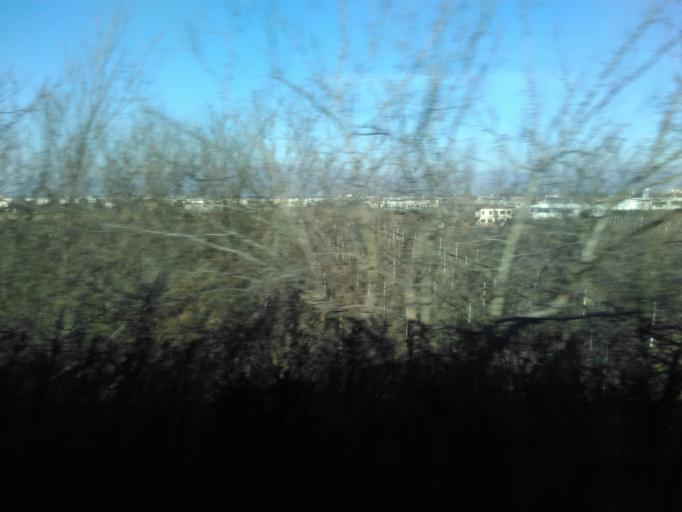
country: IT
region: Veneto
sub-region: Provincia di Verona
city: Lugagnano
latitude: 45.4275
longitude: 10.8660
